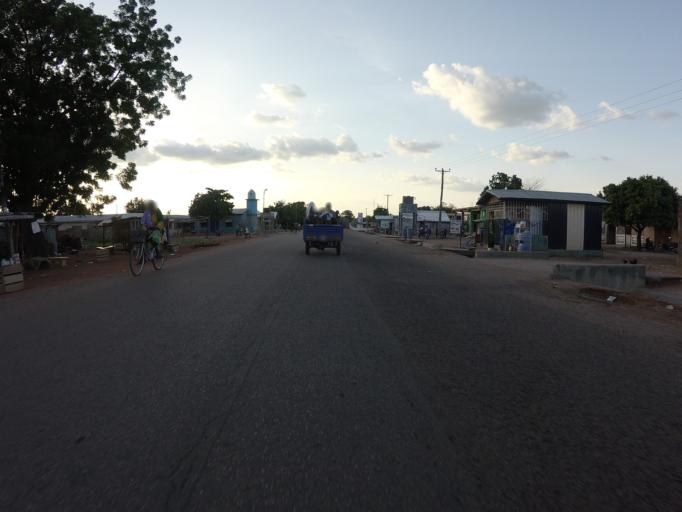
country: GH
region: Upper East
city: Navrongo
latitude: 10.9871
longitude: -1.1090
